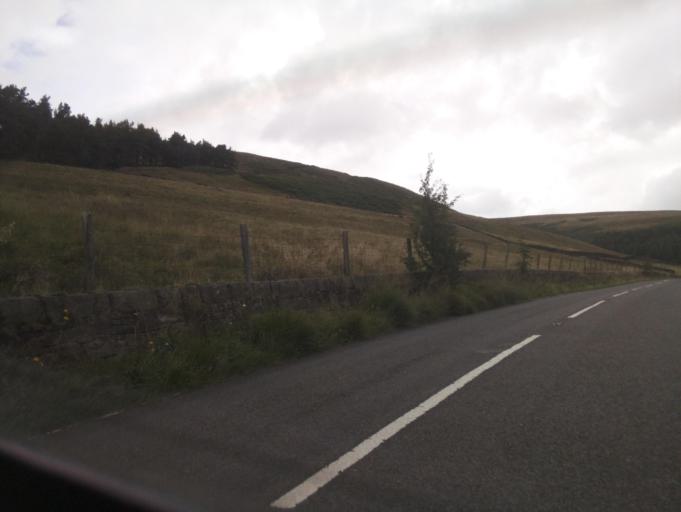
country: GB
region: England
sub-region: Kirklees
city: Meltham
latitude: 53.4975
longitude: -1.8627
